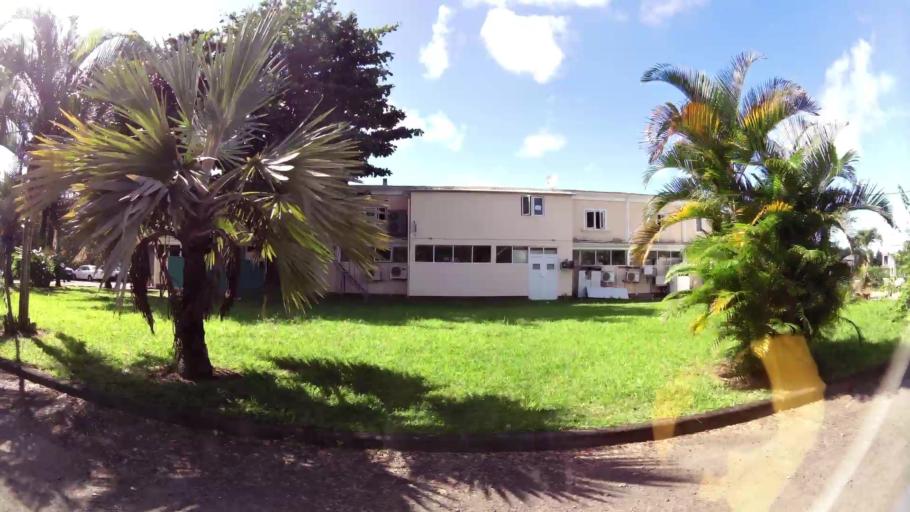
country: MU
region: Grand Port
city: Plaine Magnien
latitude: -20.4312
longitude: 57.6655
